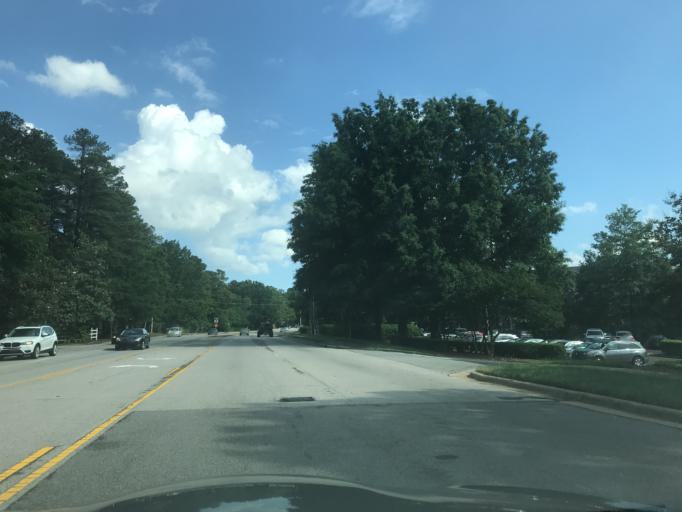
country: US
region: North Carolina
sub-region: Wake County
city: West Raleigh
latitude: 35.8696
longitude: -78.6400
